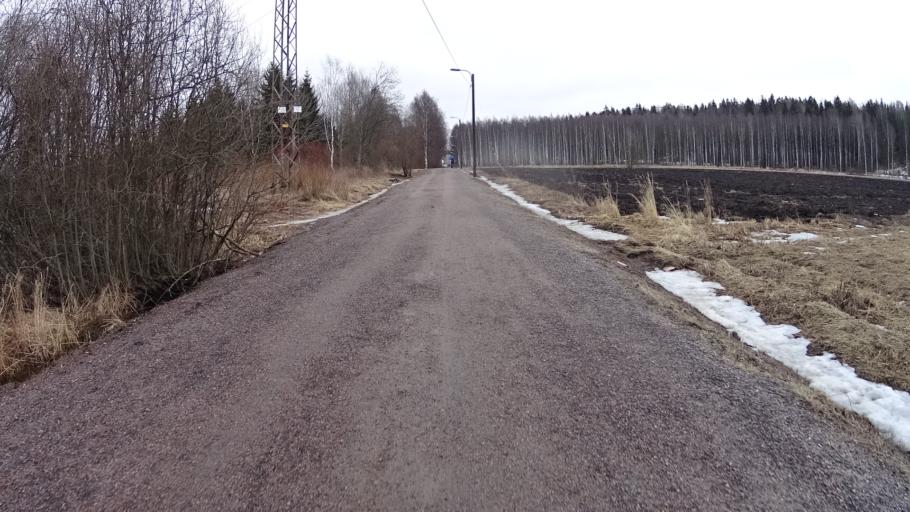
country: FI
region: Uusimaa
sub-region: Helsinki
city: Kilo
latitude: 60.2385
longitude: 24.7921
